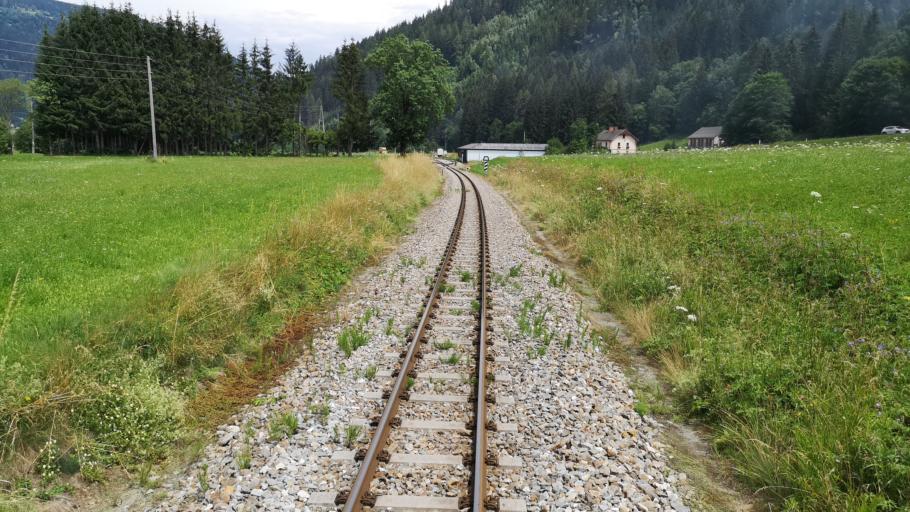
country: AT
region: Styria
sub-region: Politischer Bezirk Murau
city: Stadl an der Mur
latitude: 47.0772
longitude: 13.9230
